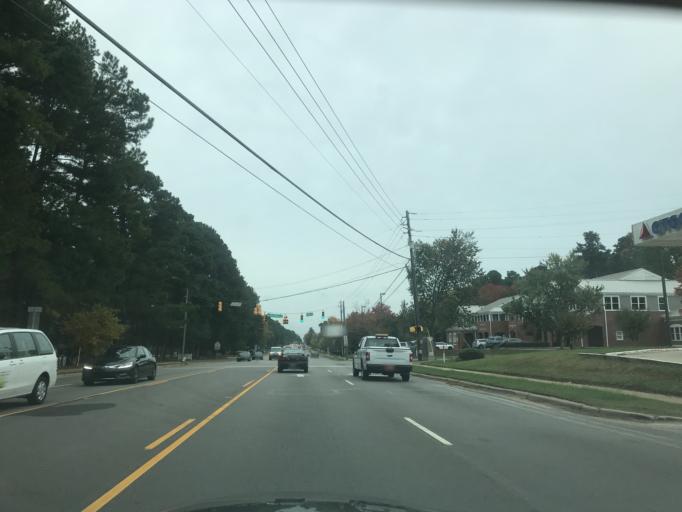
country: US
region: North Carolina
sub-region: Wake County
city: West Raleigh
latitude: 35.8803
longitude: -78.6255
